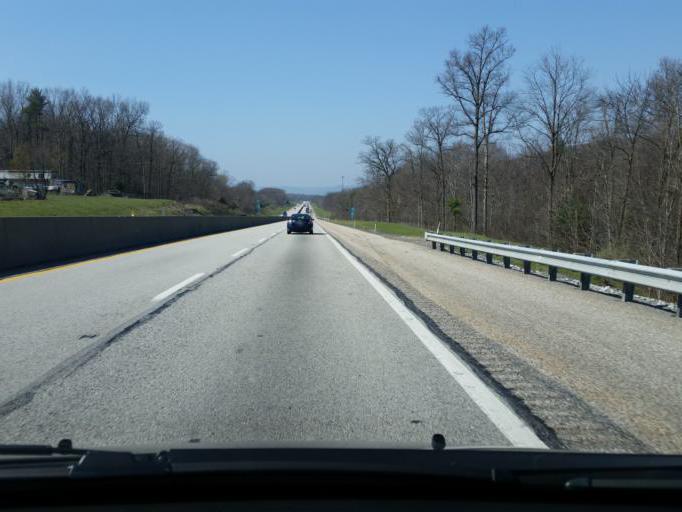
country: US
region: Pennsylvania
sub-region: Franklin County
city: Doylestown
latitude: 40.1514
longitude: -77.7150
